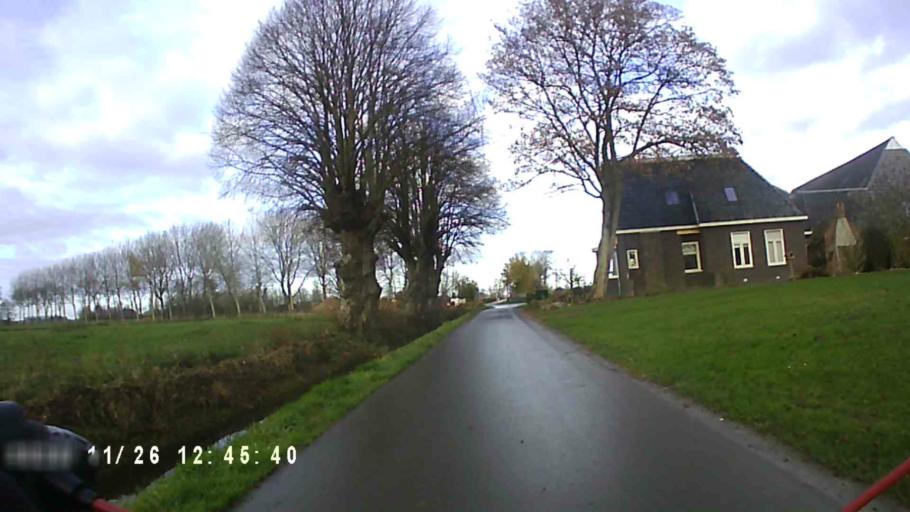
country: NL
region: Groningen
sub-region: Gemeente Appingedam
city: Appingedam
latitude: 53.3455
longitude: 6.7561
